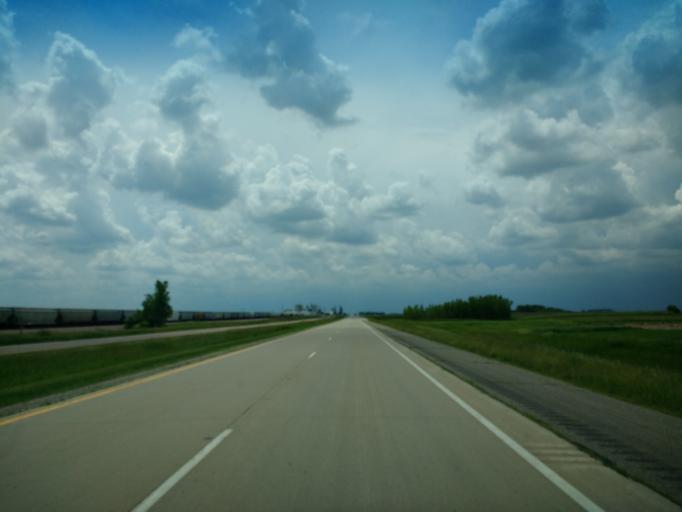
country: US
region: Minnesota
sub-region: Nobles County
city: Worthington
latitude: 43.7188
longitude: -95.4408
